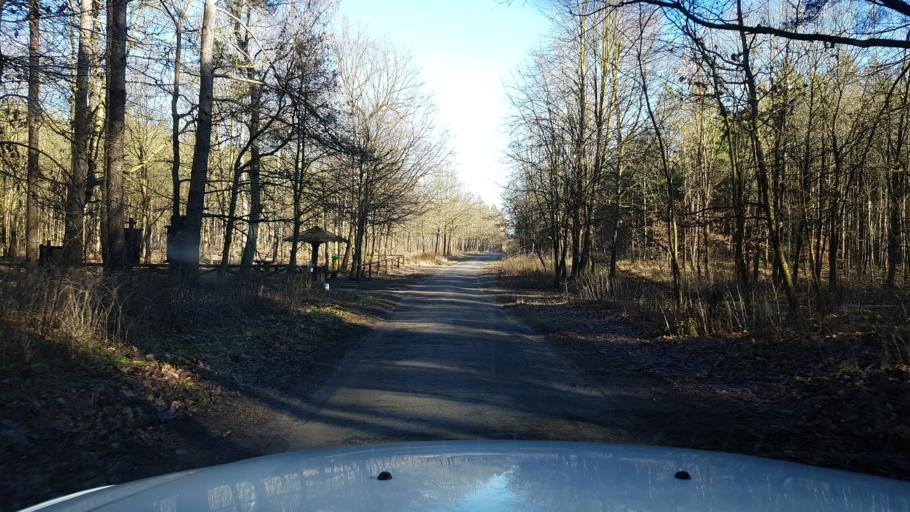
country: PL
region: West Pomeranian Voivodeship
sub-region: Powiat pyrzycki
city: Lipiany
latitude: 53.0195
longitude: 15.0050
